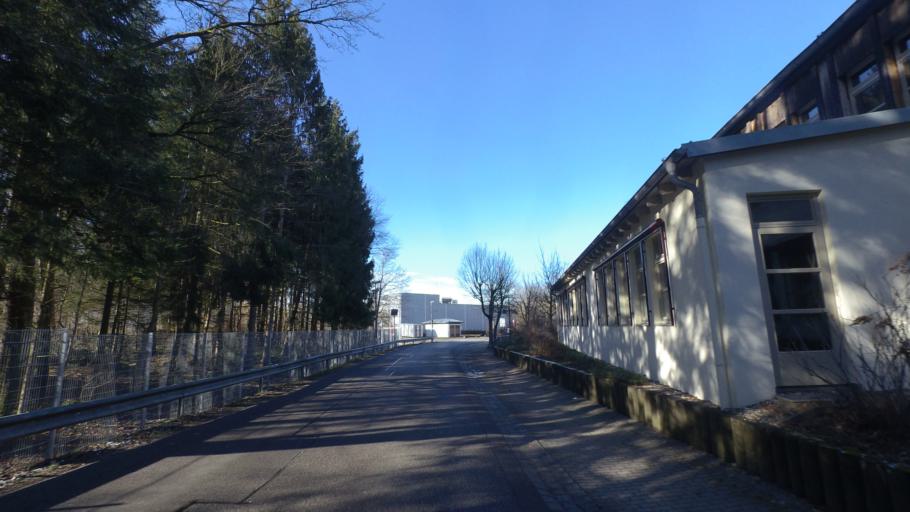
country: DE
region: Bavaria
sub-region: Upper Bavaria
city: Traunreut
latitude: 47.9588
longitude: 12.6125
